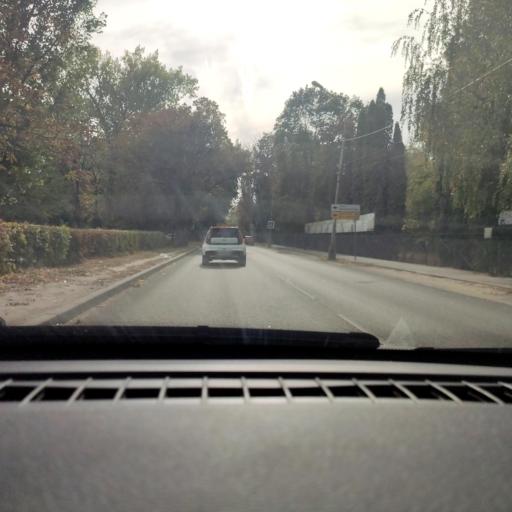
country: RU
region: Voronezj
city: Voronezh
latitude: 51.7131
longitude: 39.2244
